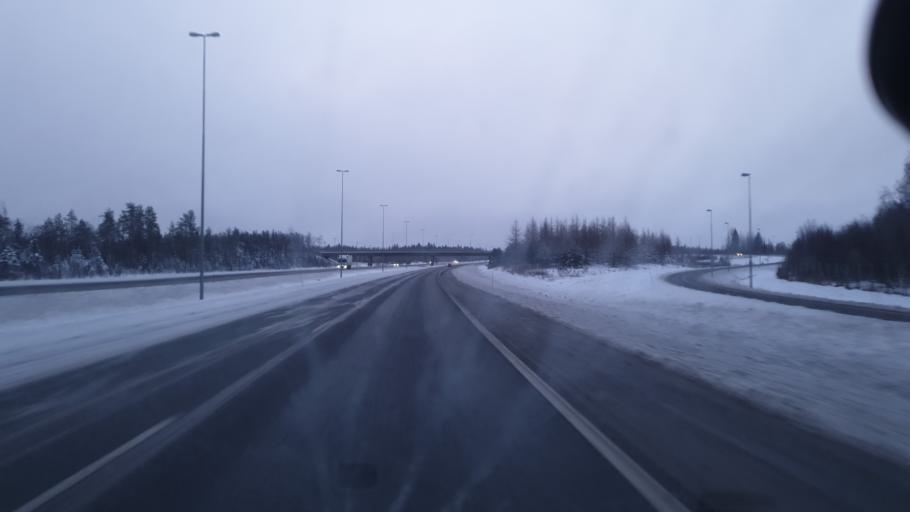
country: FI
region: Lapland
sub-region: Kemi-Tornio
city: Keminmaa
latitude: 65.8197
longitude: 24.4850
